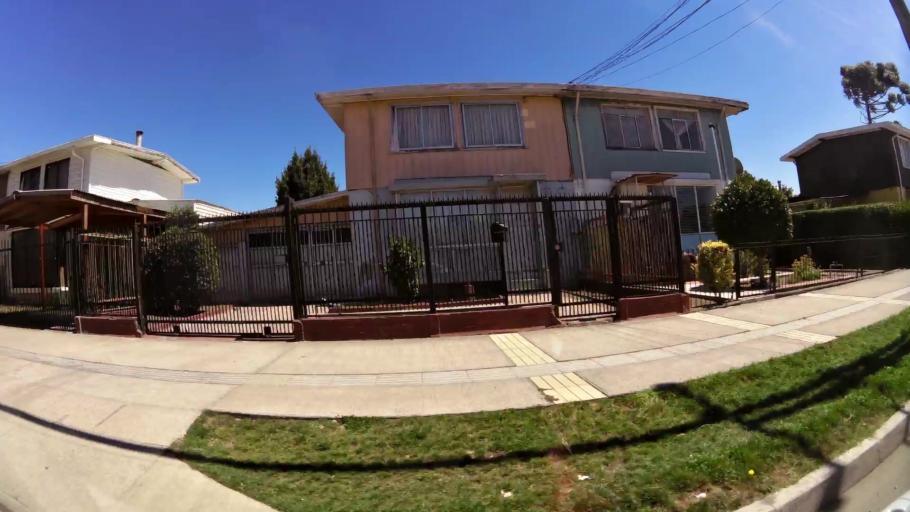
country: CL
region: Biobio
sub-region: Provincia de Concepcion
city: Talcahuano
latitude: -36.7585
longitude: -73.0913
